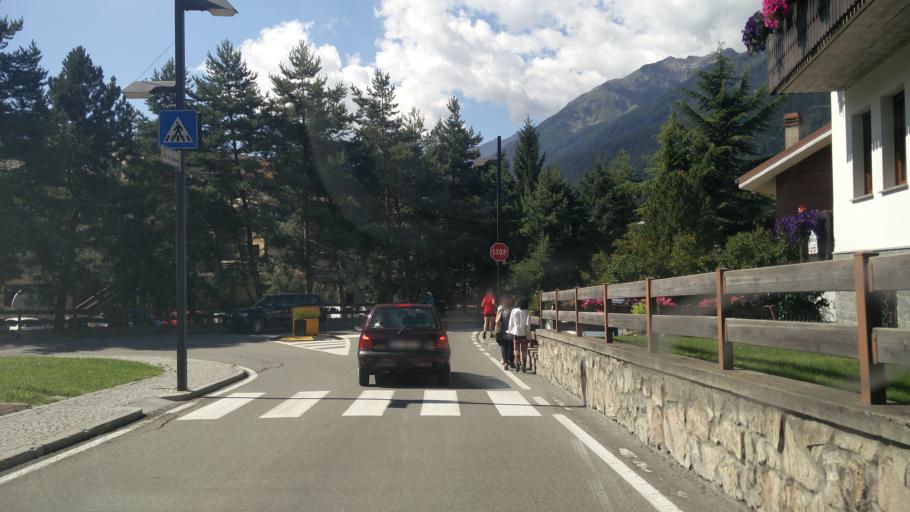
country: IT
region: Lombardy
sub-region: Provincia di Sondrio
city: Bormio
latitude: 46.4658
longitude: 10.3663
